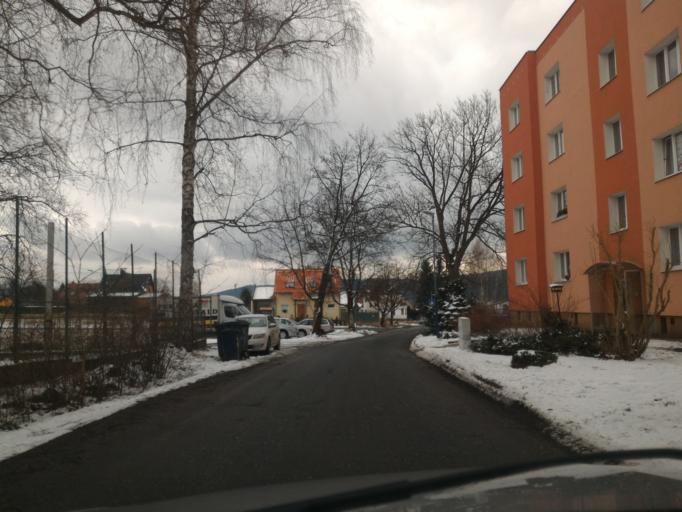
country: CZ
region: Liberecky
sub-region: Okres Jablonec nad Nisou
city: Smrzovka
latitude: 50.7341
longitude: 15.2389
